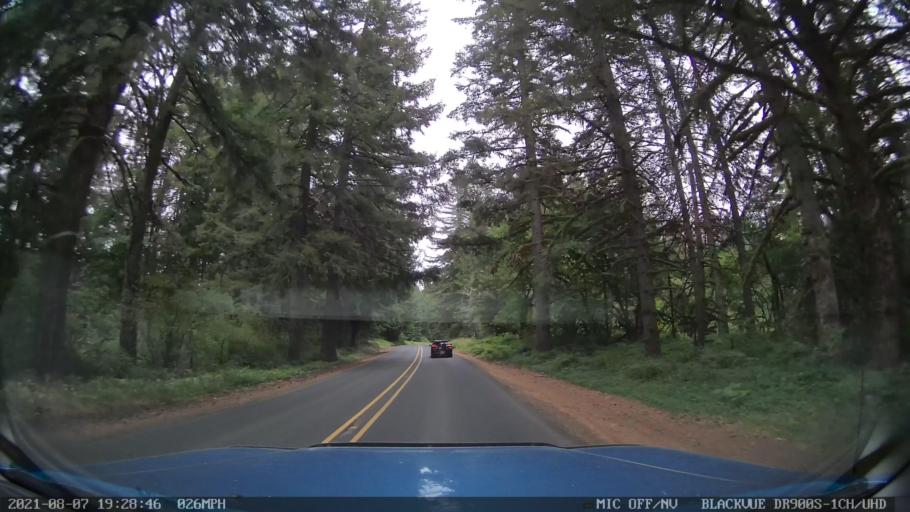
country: US
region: Oregon
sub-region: Linn County
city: Lyons
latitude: 44.8843
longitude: -122.6370
